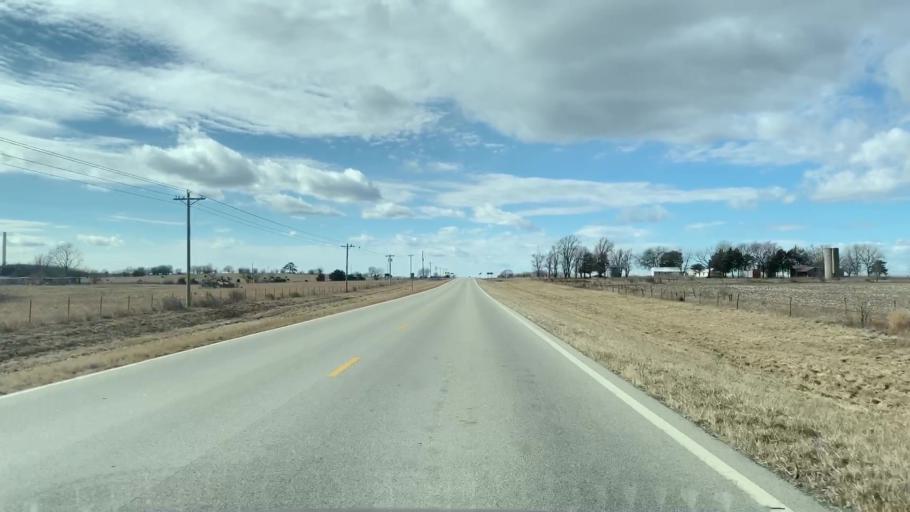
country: US
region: Kansas
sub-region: Neosho County
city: Erie
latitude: 37.5293
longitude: -95.3581
